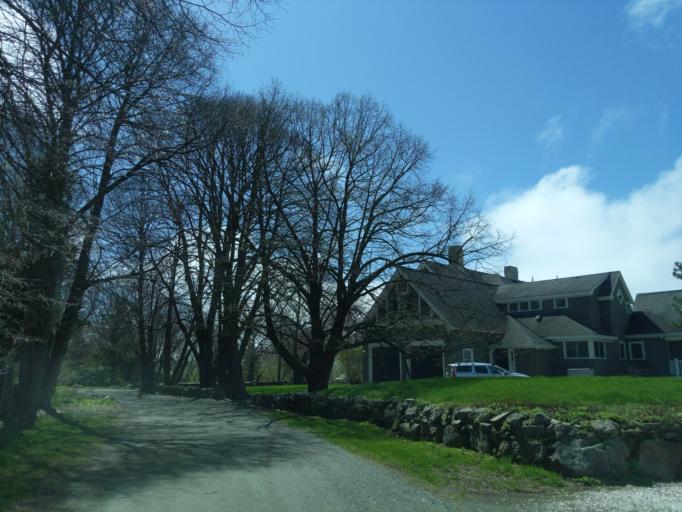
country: US
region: Massachusetts
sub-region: Essex County
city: Rockport
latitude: 42.6375
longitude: -70.6036
